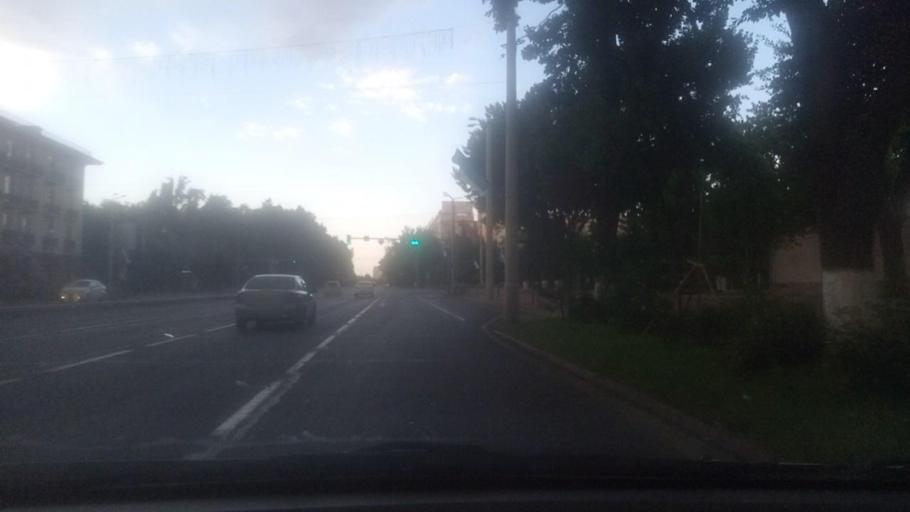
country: UZ
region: Toshkent Shahri
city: Tashkent
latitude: 41.3104
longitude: 69.2678
